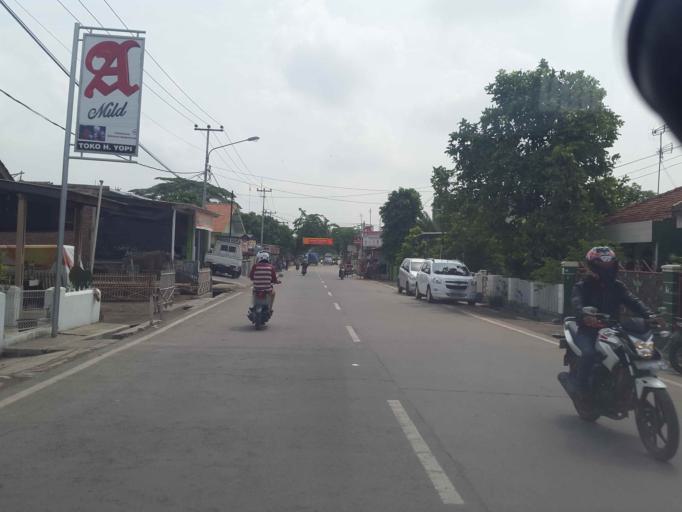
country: ID
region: West Java
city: Rengasdengklok
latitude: -6.2941
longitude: 107.3301
